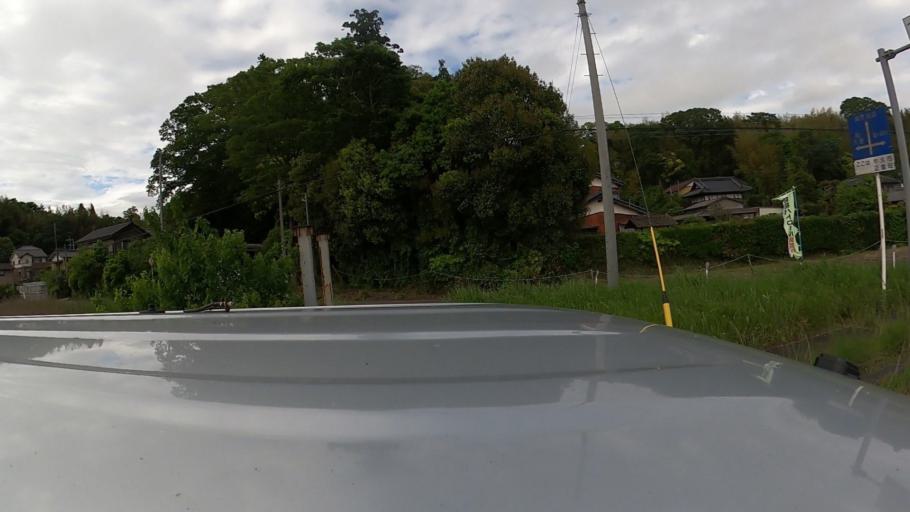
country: JP
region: Ibaraki
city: Ryugasaki
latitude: 35.9533
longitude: 140.2209
